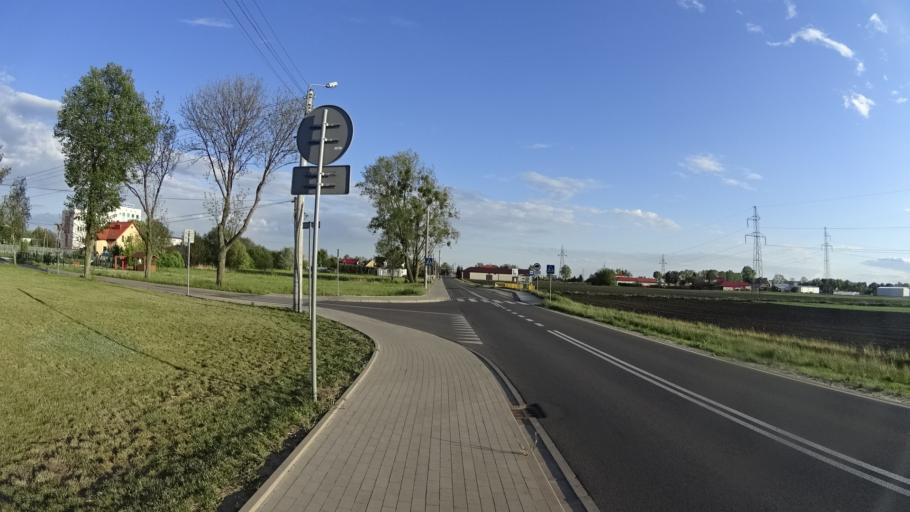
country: PL
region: Masovian Voivodeship
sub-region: Powiat warszawski zachodni
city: Jozefow
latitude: 52.2155
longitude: 20.7403
